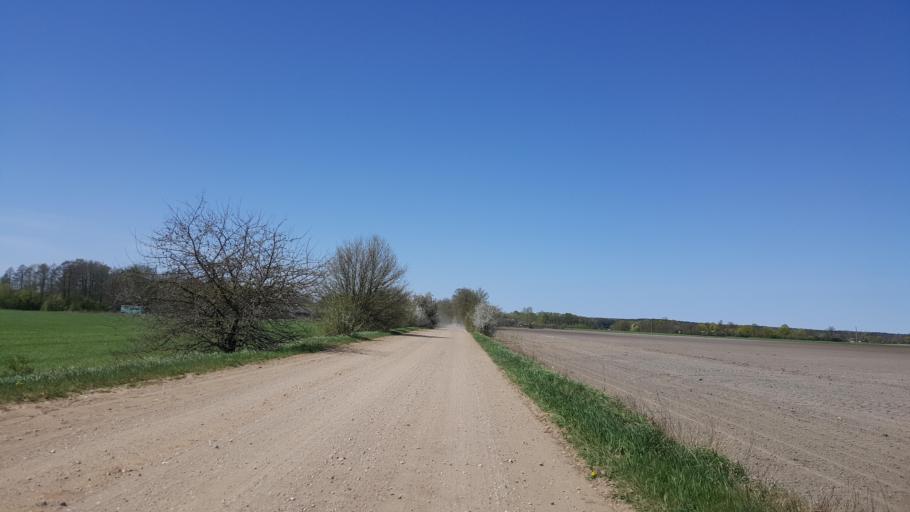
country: BY
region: Brest
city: Kamyanyets
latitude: 52.3284
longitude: 23.7645
